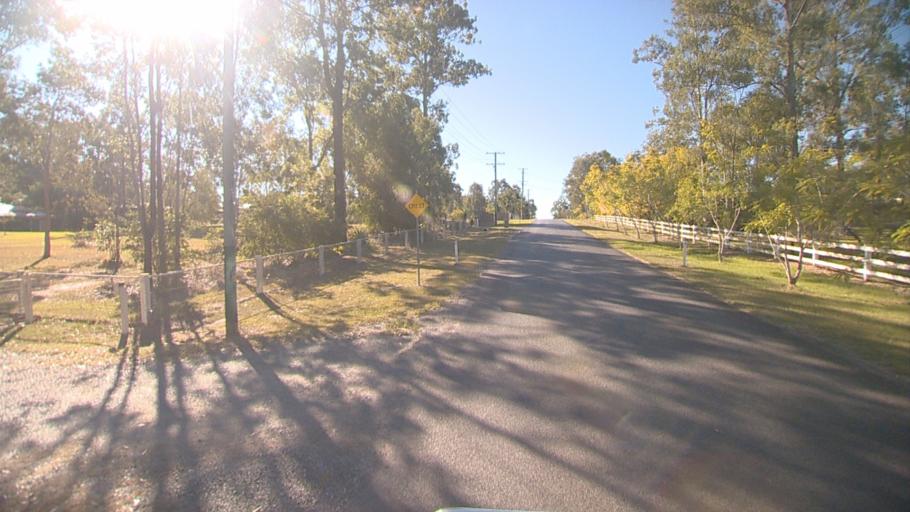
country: AU
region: Queensland
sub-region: Logan
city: Park Ridge South
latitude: -27.7284
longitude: 153.0201
